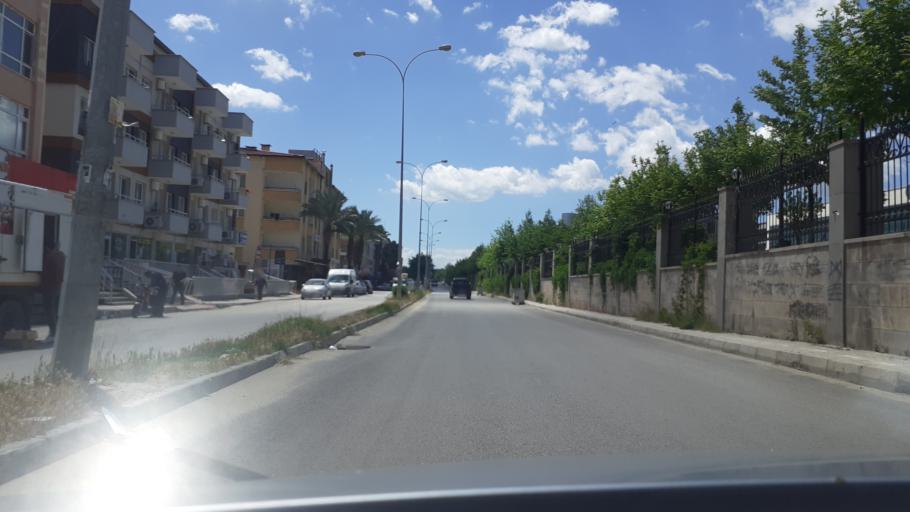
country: TR
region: Hatay
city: Anayazi
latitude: 36.3362
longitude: 36.2000
